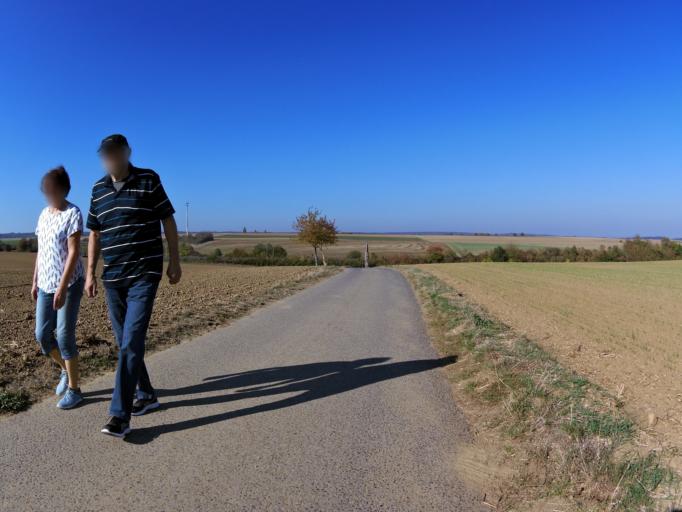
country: DE
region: Bavaria
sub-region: Regierungsbezirk Unterfranken
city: Geroldshausen
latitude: 49.6931
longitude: 9.9164
